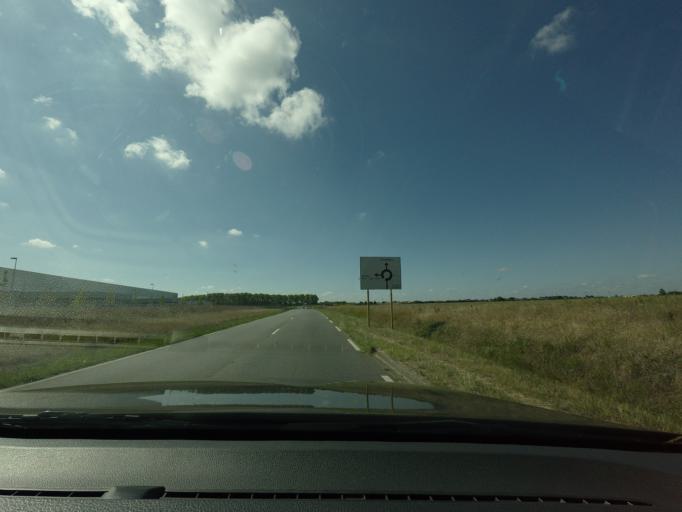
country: FR
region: Midi-Pyrenees
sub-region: Departement de la Haute-Garonne
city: Cornebarrieu
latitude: 43.6323
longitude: 1.3320
